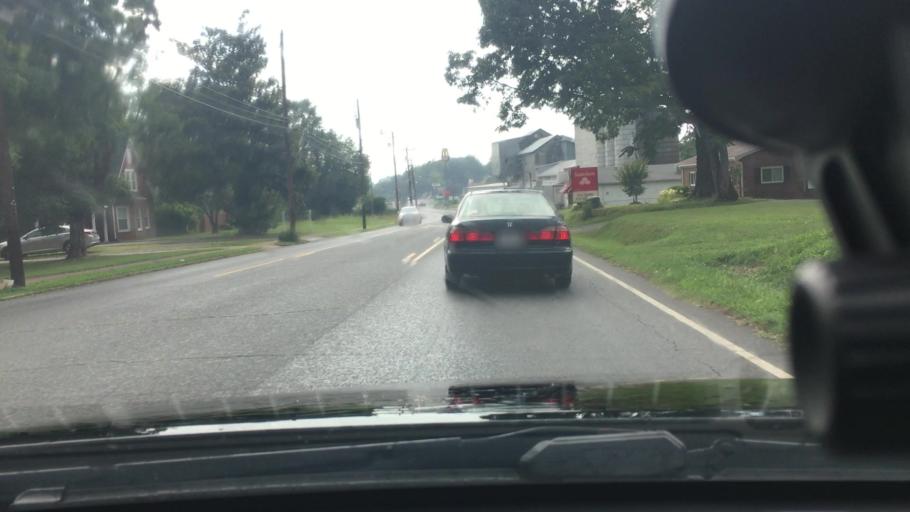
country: US
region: North Carolina
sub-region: Rutherford County
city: Spindale
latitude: 35.3605
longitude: -81.9372
